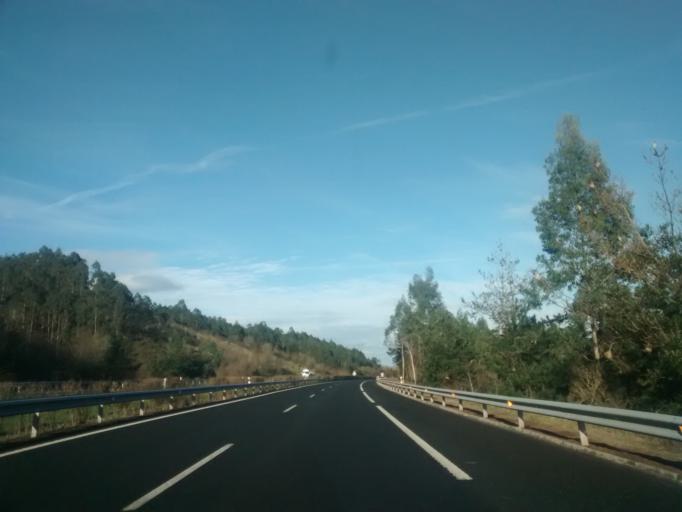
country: ES
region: Cantabria
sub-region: Provincia de Cantabria
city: Cabezon de la Sal
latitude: 43.3241
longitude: -4.2949
